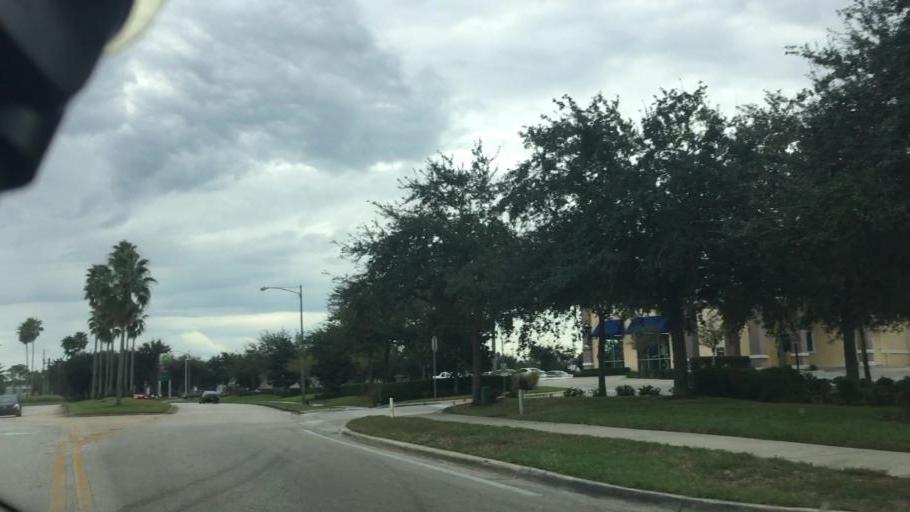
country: US
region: Florida
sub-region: Orange County
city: Alafaya
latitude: 28.6079
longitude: -81.2101
